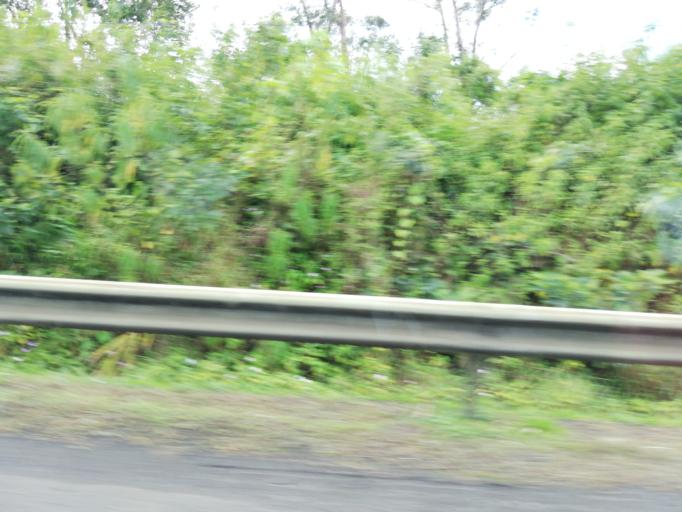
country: MU
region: Plaines Wilhems
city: Midlands
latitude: -20.3430
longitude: 57.5674
